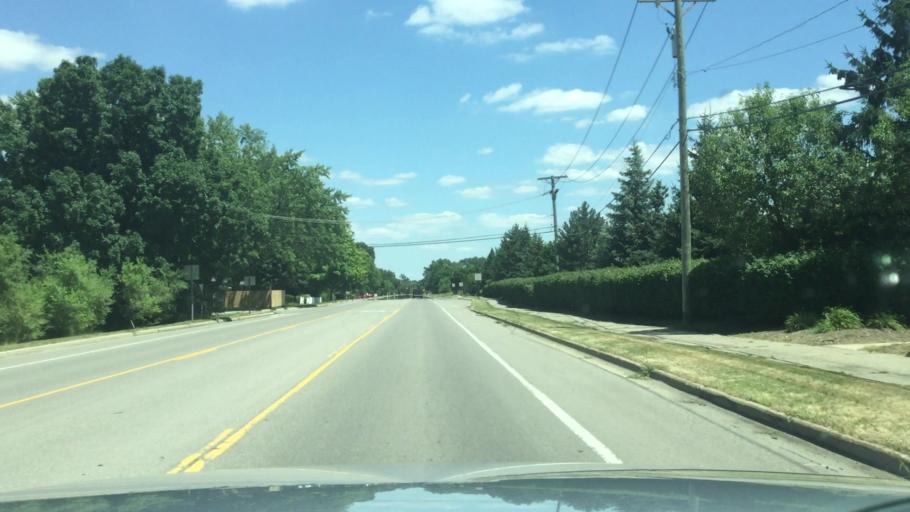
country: US
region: Michigan
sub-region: Washtenaw County
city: Ypsilanti
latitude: 42.2136
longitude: -83.5571
